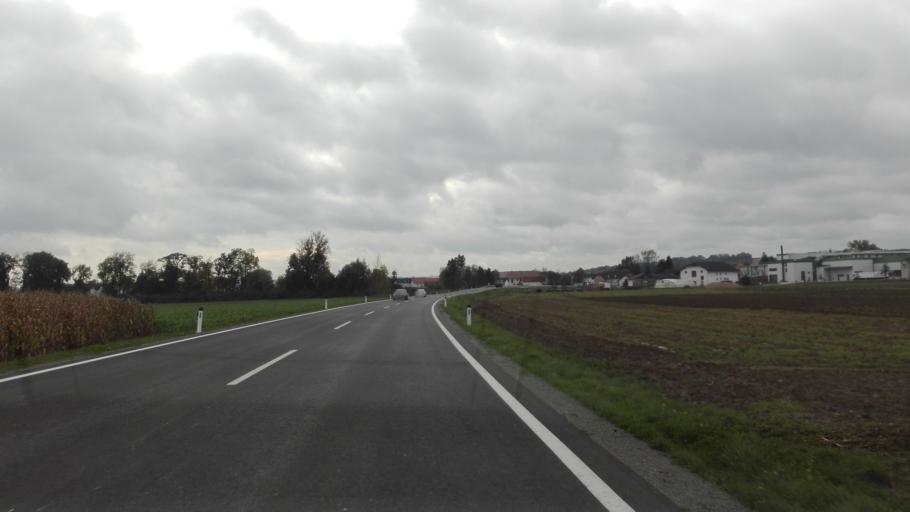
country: AT
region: Upper Austria
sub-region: Politischer Bezirk Urfahr-Umgebung
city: Feldkirchen an der Donau
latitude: 48.3144
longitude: 14.0074
